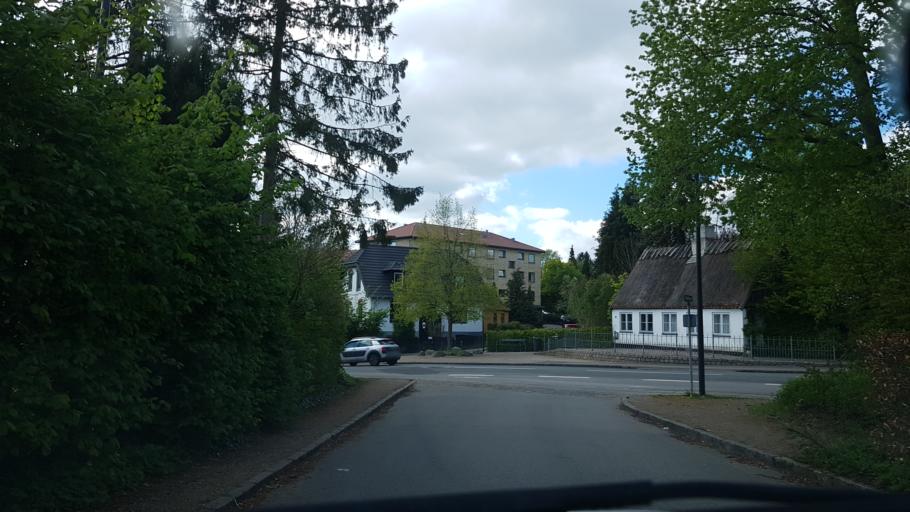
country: DK
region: Capital Region
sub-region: Rudersdal Kommune
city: Holte
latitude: 55.8169
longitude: 12.4889
